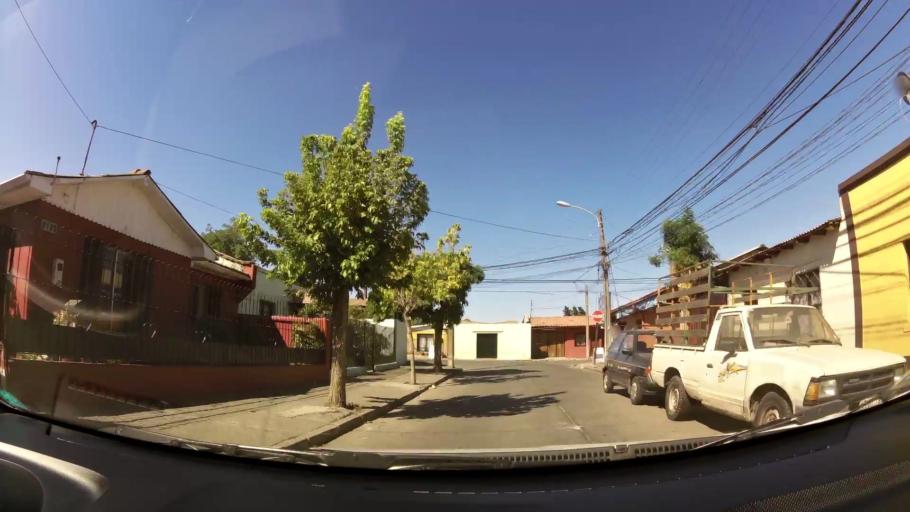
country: CL
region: O'Higgins
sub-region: Provincia de Cachapoal
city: Rancagua
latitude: -34.1801
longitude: -70.7506
